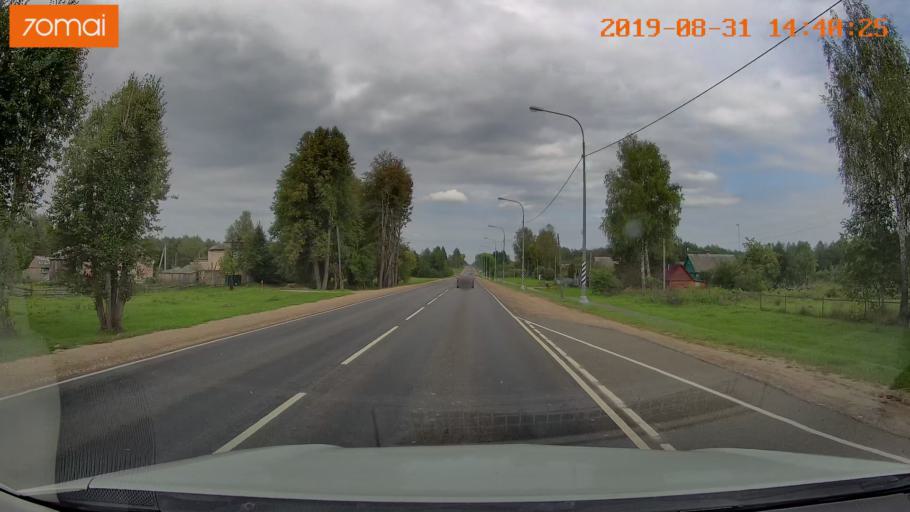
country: RU
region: Smolensk
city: Yekimovichi
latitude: 54.1971
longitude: 33.5711
